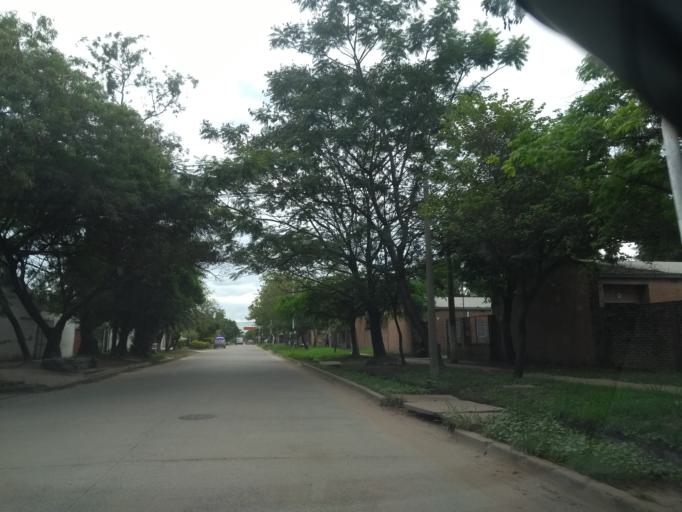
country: AR
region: Chaco
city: Presidencia Roque Saenz Pena
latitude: -26.7997
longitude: -60.4483
